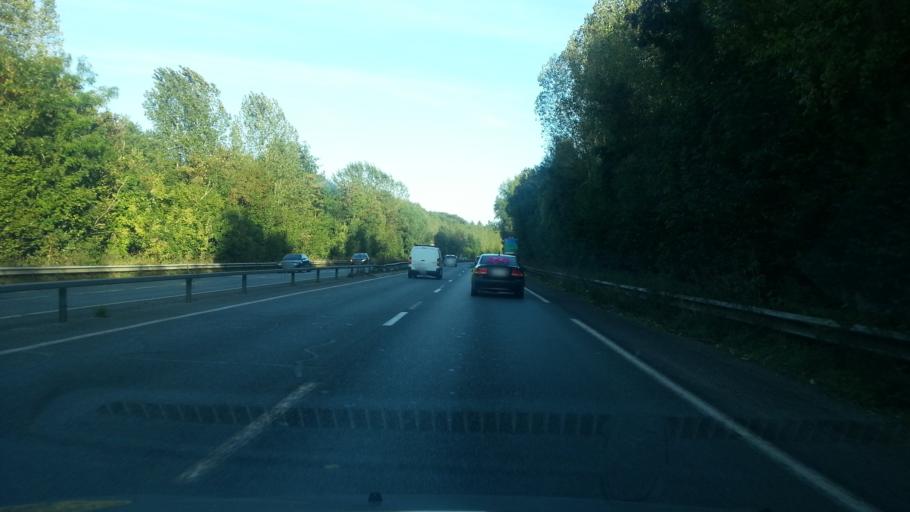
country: FR
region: Picardie
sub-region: Departement de l'Oise
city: Fitz-James
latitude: 49.3885
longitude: 2.4175
